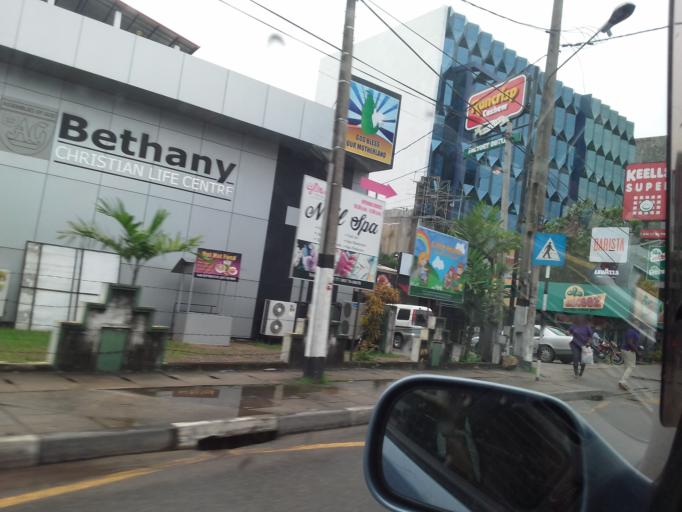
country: LK
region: Western
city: Pita Kotte
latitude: 6.9068
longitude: 79.9018
